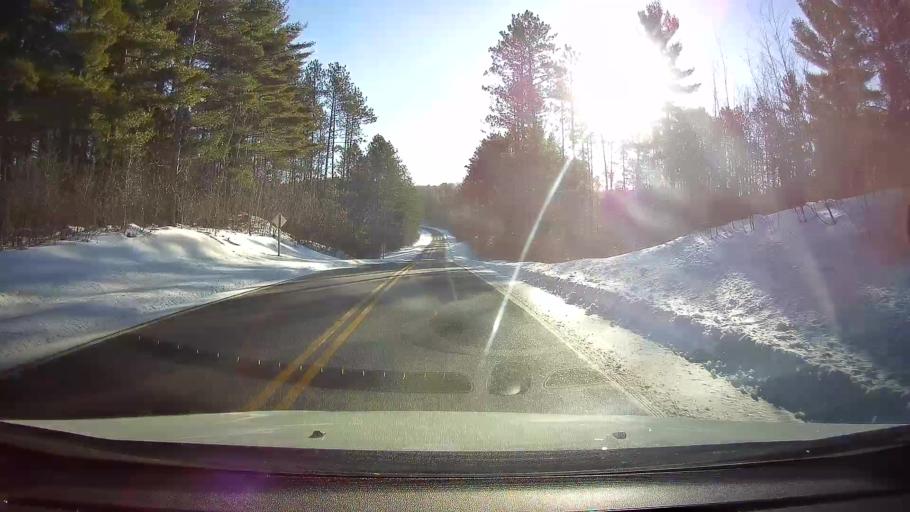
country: US
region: Wisconsin
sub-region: Sawyer County
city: Little Round Lake
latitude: 46.1109
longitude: -91.3057
